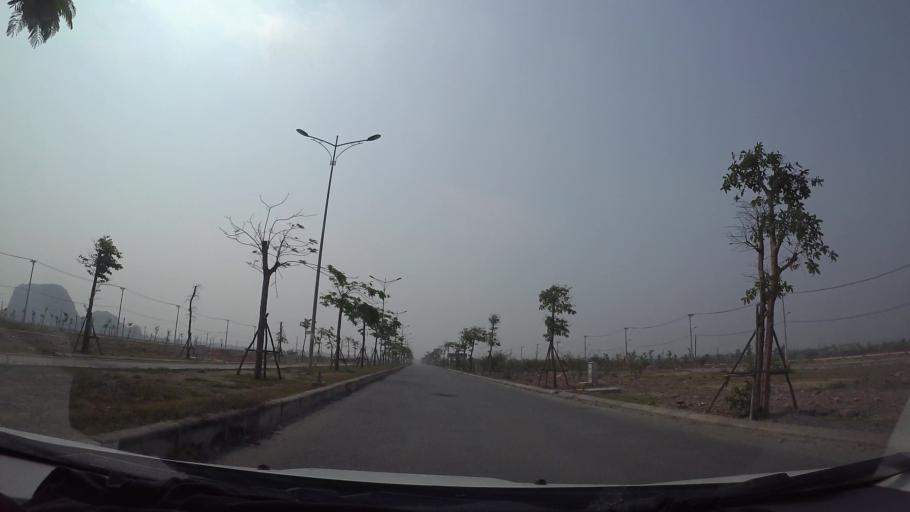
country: VN
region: Da Nang
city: Ngu Hanh Son
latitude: 16.0045
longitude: 108.2461
